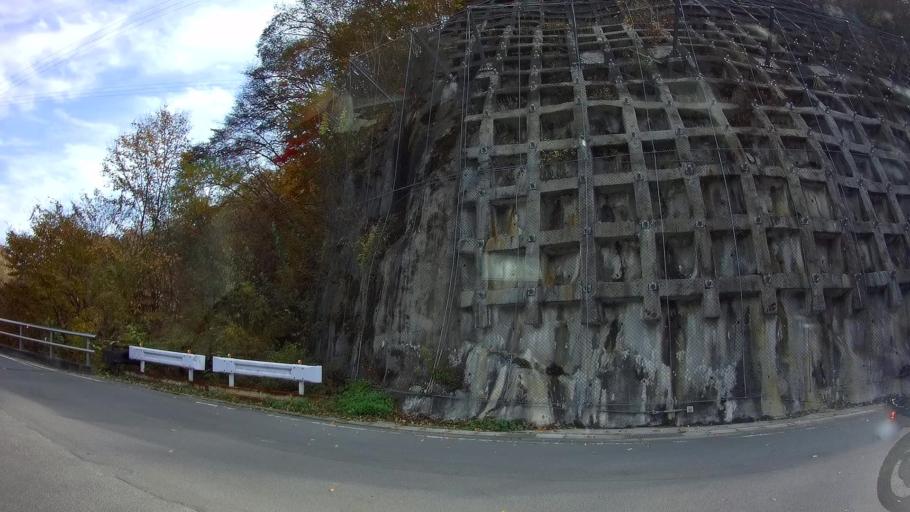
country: JP
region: Gunma
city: Nakanojomachi
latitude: 36.6279
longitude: 138.6336
